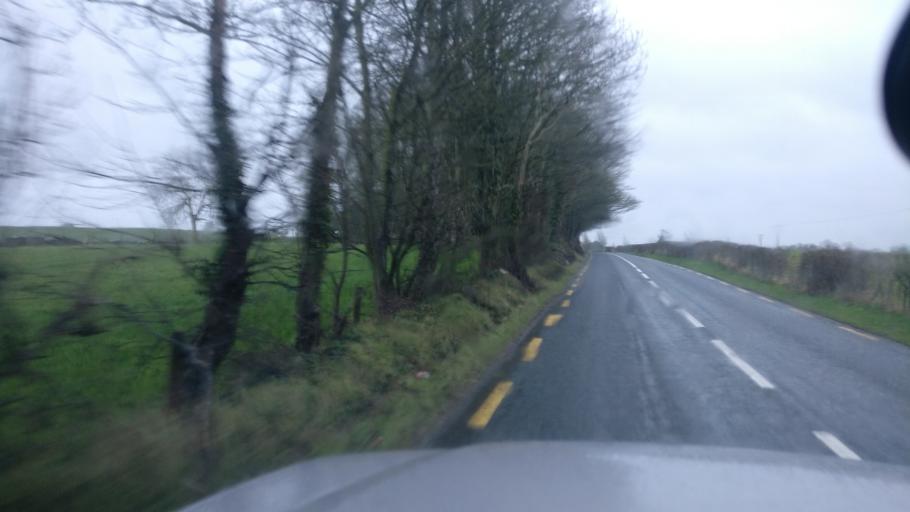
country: IE
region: Connaught
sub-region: County Galway
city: Ballinasloe
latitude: 53.2575
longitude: -8.1827
